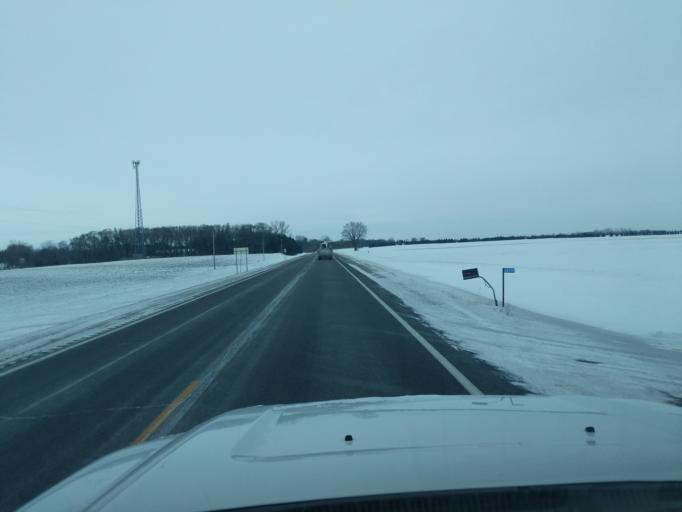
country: US
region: Minnesota
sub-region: Redwood County
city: Redwood Falls
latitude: 44.5757
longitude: -94.9946
